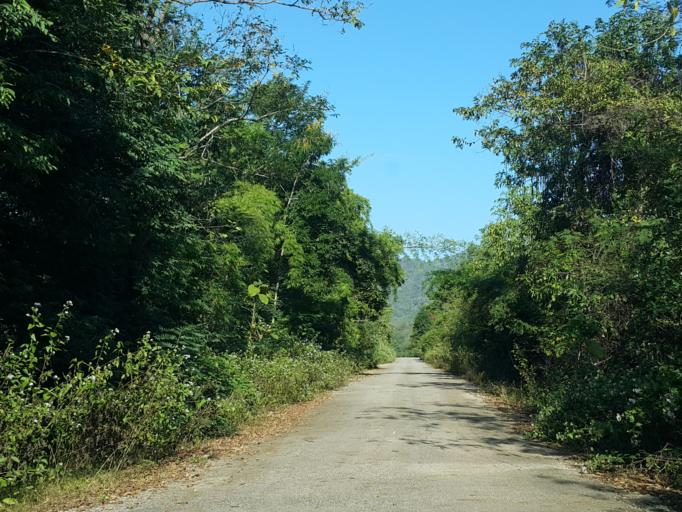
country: TH
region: Lampang
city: Mae Mo
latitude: 18.3036
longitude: 99.6629
